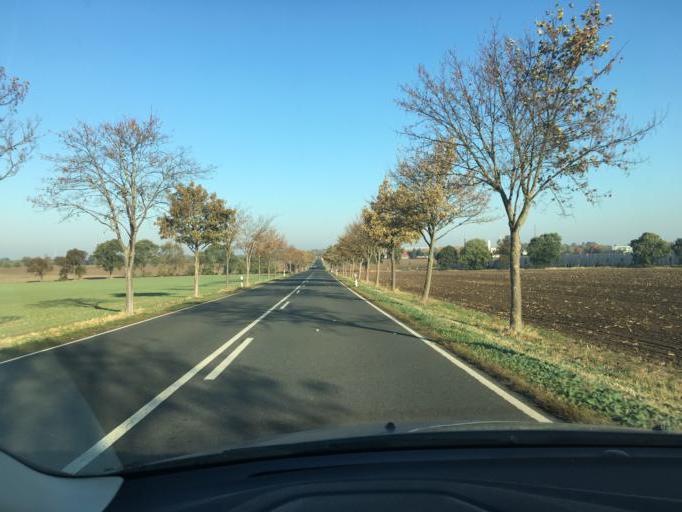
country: DE
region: Saxony-Anhalt
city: Wanzleben
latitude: 52.0454
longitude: 11.4583
